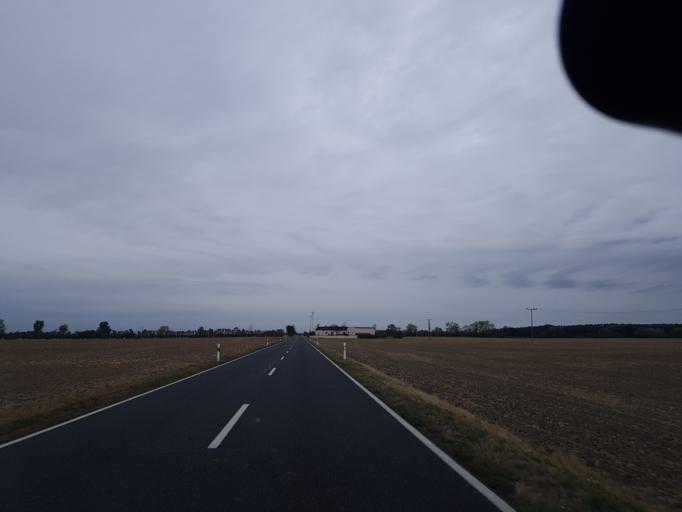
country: DE
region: Saxony-Anhalt
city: Prettin
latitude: 51.6750
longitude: 12.9113
